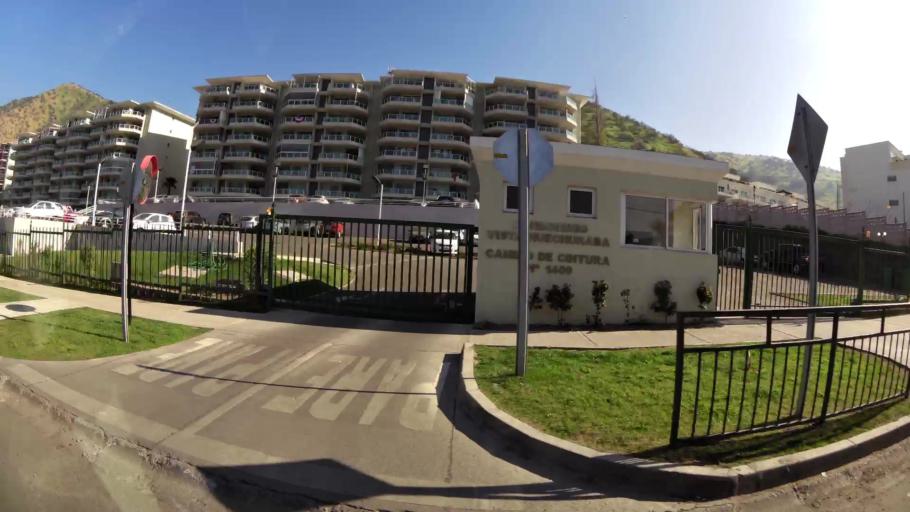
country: CL
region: Santiago Metropolitan
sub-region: Provincia de Chacabuco
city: Chicureo Abajo
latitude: -33.3392
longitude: -70.6688
